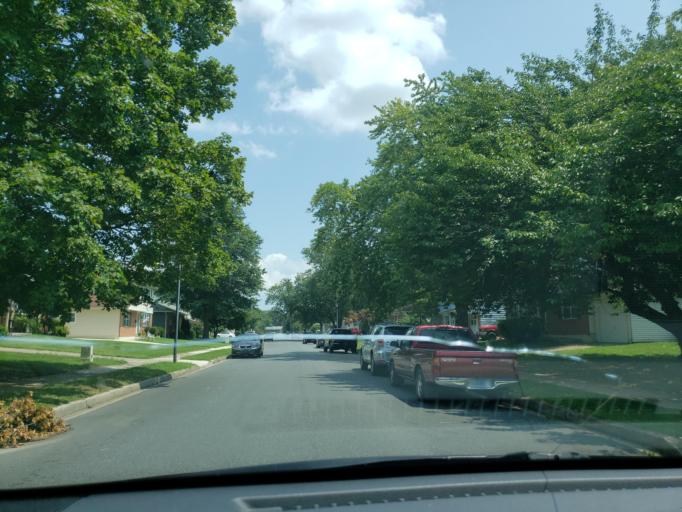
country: US
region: Delaware
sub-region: Kent County
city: Rodney Village
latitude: 39.1349
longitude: -75.5386
